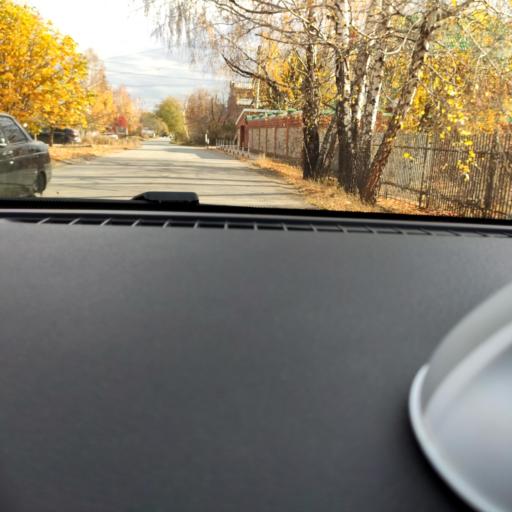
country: RU
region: Samara
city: Petra-Dubrava
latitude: 53.2490
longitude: 50.3134
